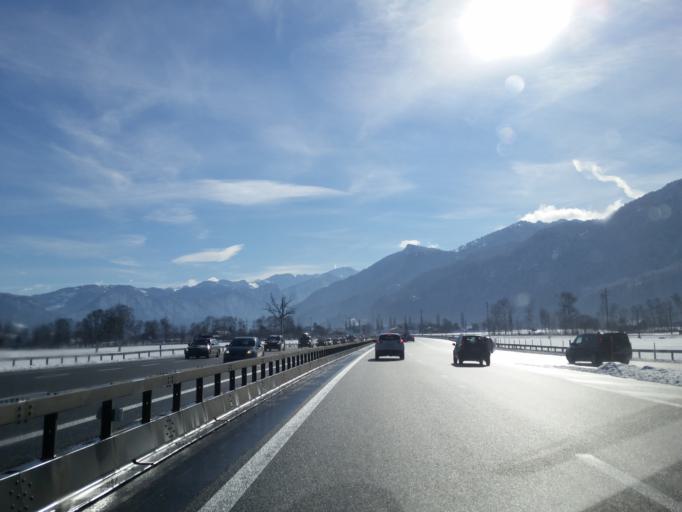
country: CH
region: Saint Gallen
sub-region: Wahlkreis Sarganserland
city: Sargans
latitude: 47.0351
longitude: 9.4650
